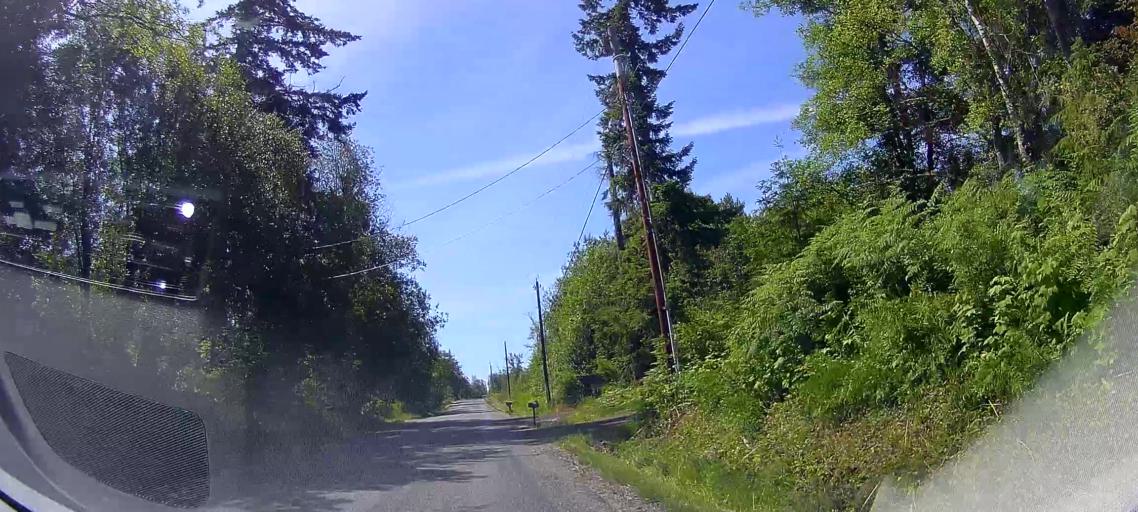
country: US
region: Washington
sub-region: Skagit County
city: Sedro-Woolley
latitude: 48.5412
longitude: -122.2485
